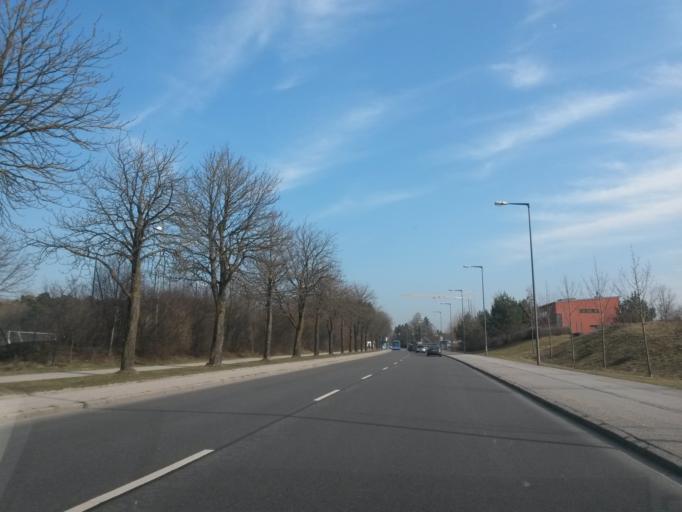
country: DE
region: Bavaria
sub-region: Upper Bavaria
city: Neubiberg
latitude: 48.0915
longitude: 11.6595
